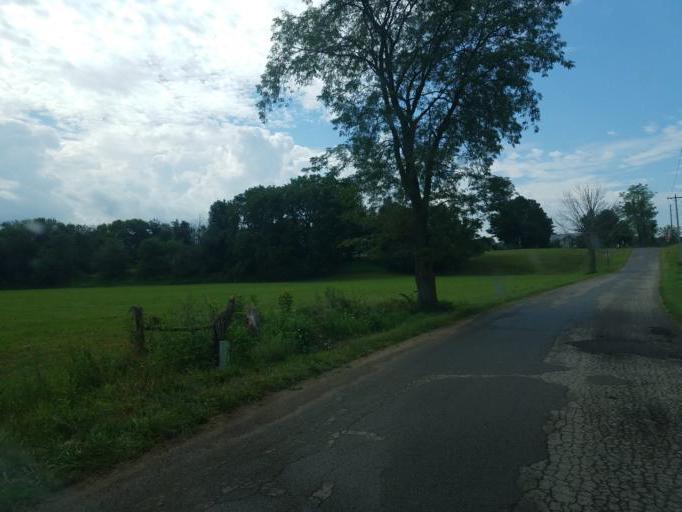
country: US
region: Ohio
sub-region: Knox County
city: Fredericktown
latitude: 40.4577
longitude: -82.6561
